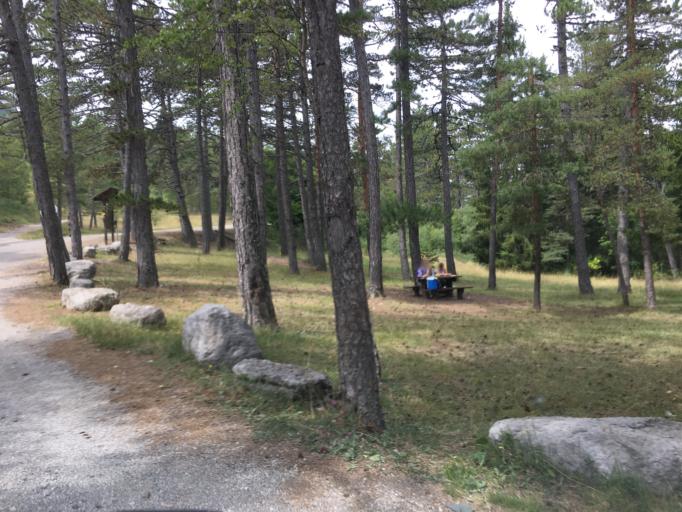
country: FR
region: Provence-Alpes-Cote d'Azur
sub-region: Departement des Alpes-de-Haute-Provence
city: Digne-les-Bains
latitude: 44.2153
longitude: 6.1476
